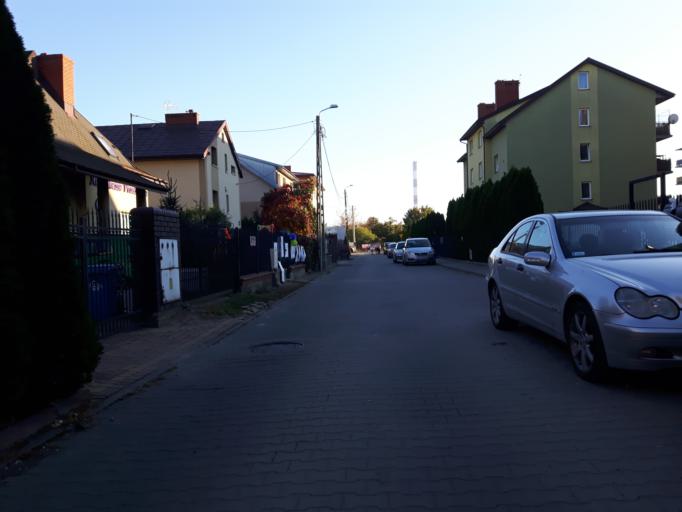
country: PL
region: Masovian Voivodeship
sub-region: Powiat wolominski
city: Zabki
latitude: 52.2857
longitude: 21.1273
